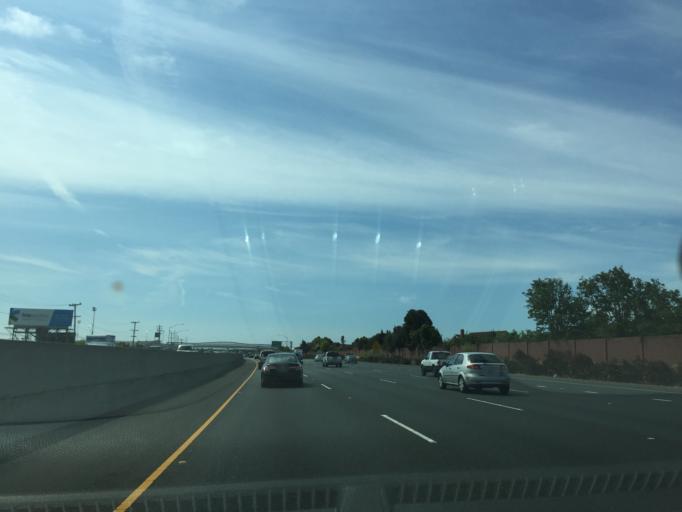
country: US
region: California
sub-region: San Mateo County
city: Belmont
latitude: 37.5318
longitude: -122.2762
